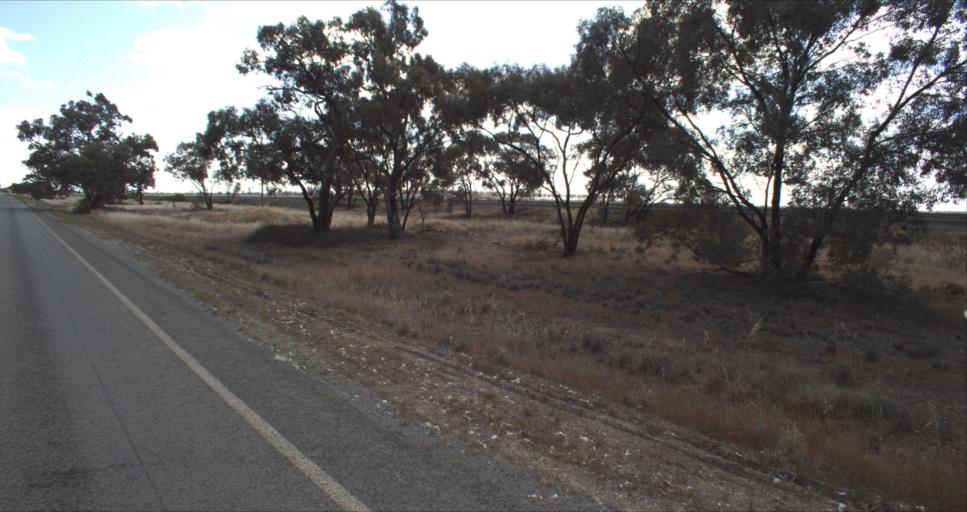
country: AU
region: New South Wales
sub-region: Murrumbidgee Shire
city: Darlington Point
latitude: -34.5719
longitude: 146.1670
